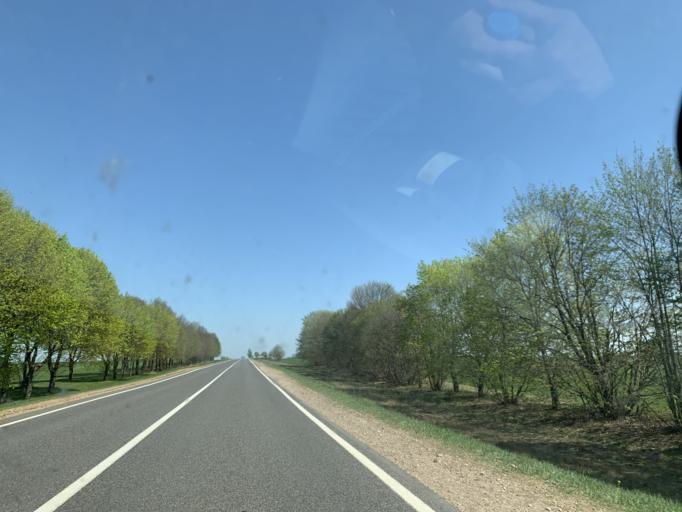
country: BY
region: Minsk
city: Nyasvizh
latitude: 53.2409
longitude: 26.8542
